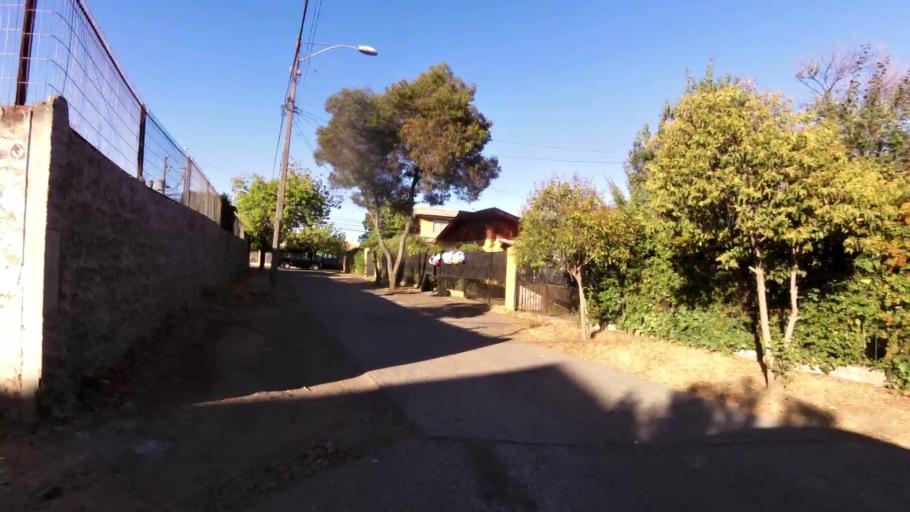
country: CL
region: O'Higgins
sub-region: Provincia de Cachapoal
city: Rancagua
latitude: -34.1707
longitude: -70.7179
